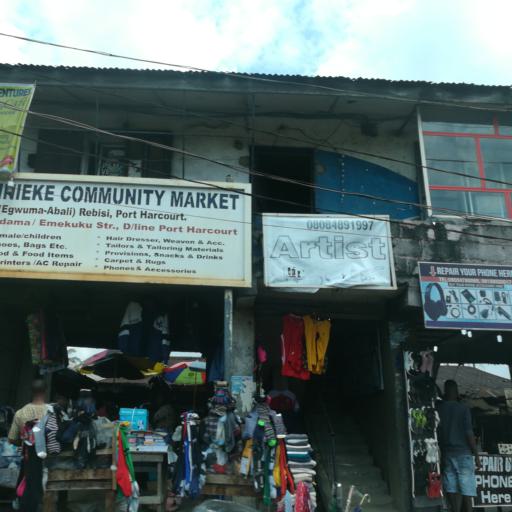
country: NG
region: Rivers
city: Port Harcourt
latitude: 4.8051
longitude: 7.0043
